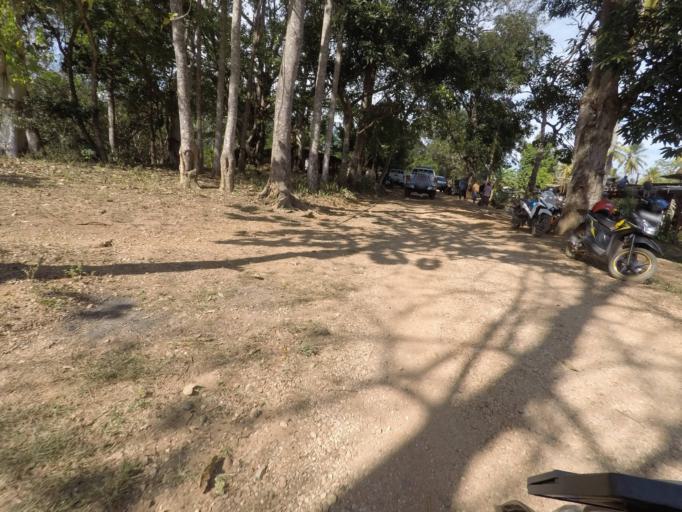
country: TL
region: Bobonaro
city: Maliana
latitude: -8.9599
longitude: 125.2184
